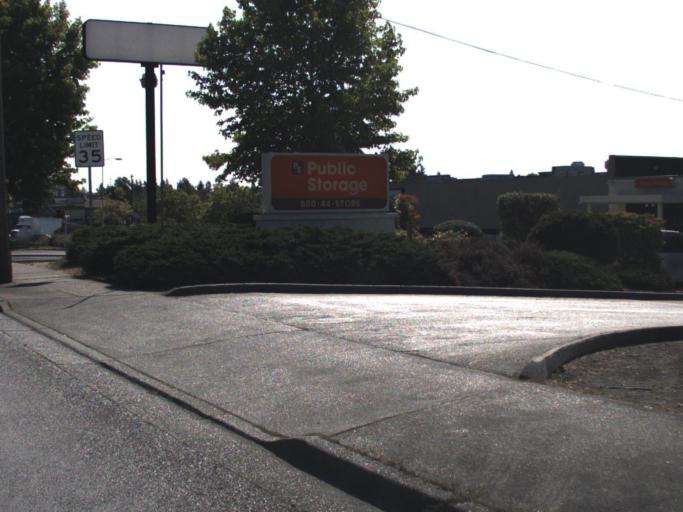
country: US
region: Washington
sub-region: Snohomish County
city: Alderwood Manor
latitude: 47.8210
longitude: -122.2957
